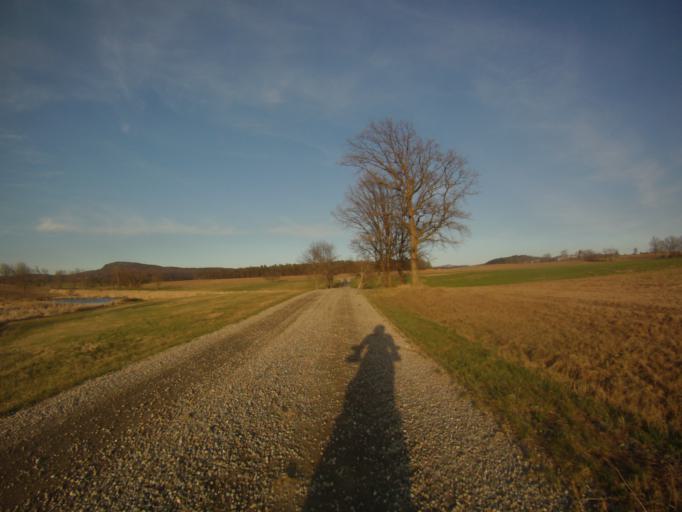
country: US
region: Vermont
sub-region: Addison County
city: Vergennes
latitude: 44.1012
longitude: -73.2706
